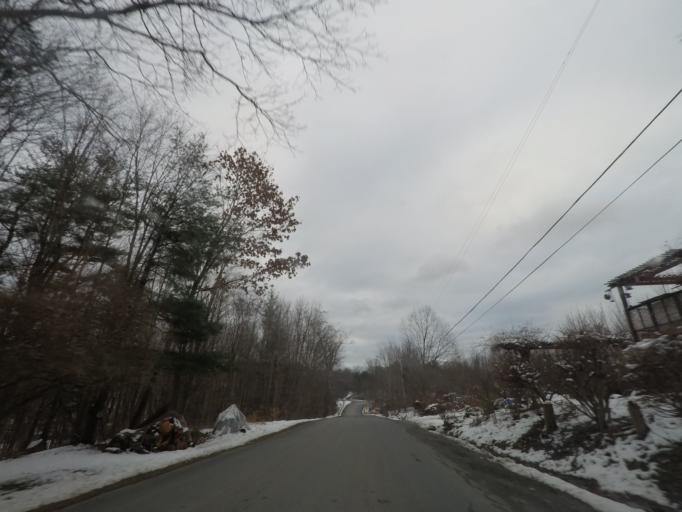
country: US
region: New York
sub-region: Rensselaer County
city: Averill Park
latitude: 42.6402
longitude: -73.5377
